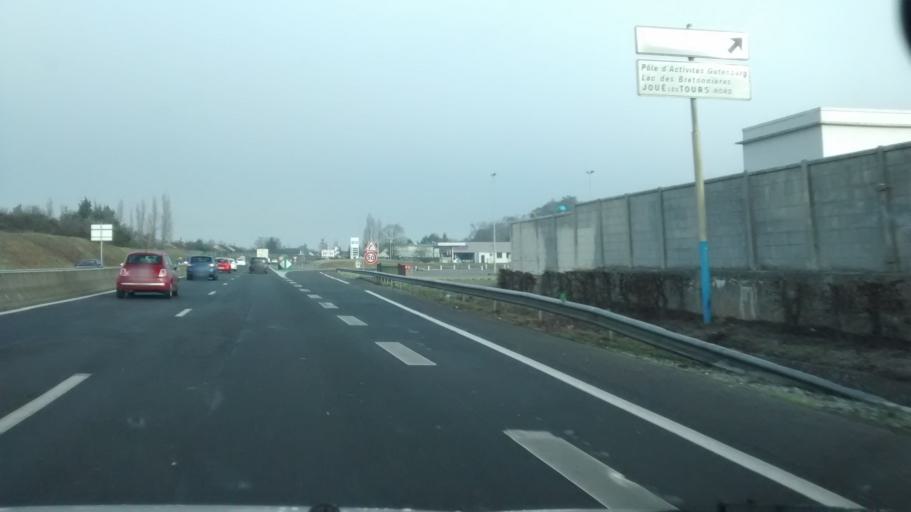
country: FR
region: Centre
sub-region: Departement d'Indre-et-Loire
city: Joue-les-Tours
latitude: 47.3565
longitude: 0.6459
